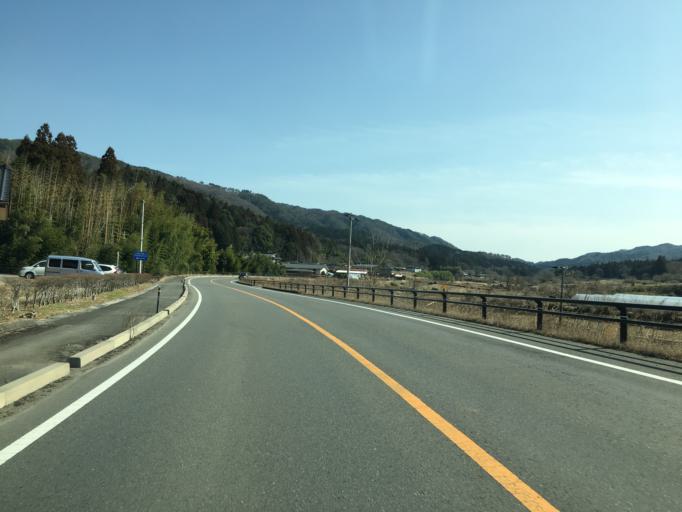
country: JP
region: Ibaraki
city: Daigo
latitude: 36.8342
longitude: 140.4514
